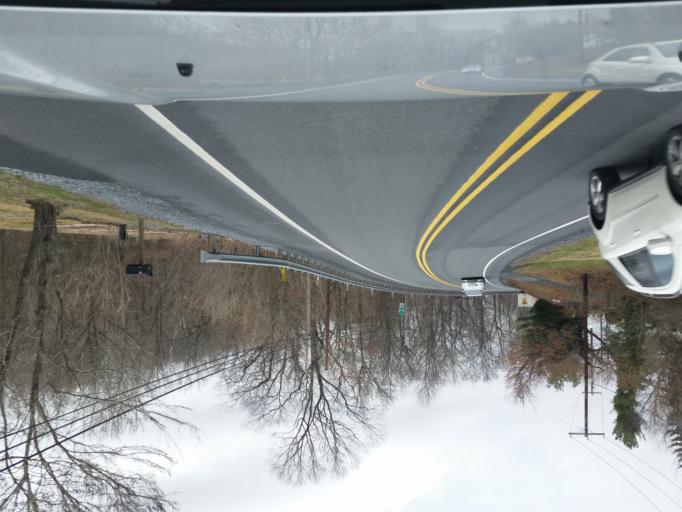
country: US
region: Pennsylvania
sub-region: Dauphin County
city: Rutherford
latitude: 40.2723
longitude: -76.7481
